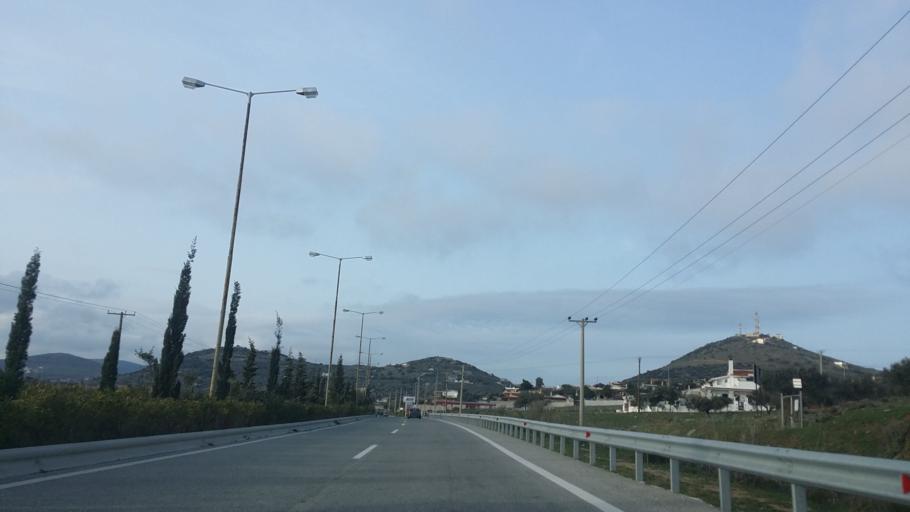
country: GR
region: Attica
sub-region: Nomarchia Anatolikis Attikis
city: Lavrio
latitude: 37.7838
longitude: 24.0575
